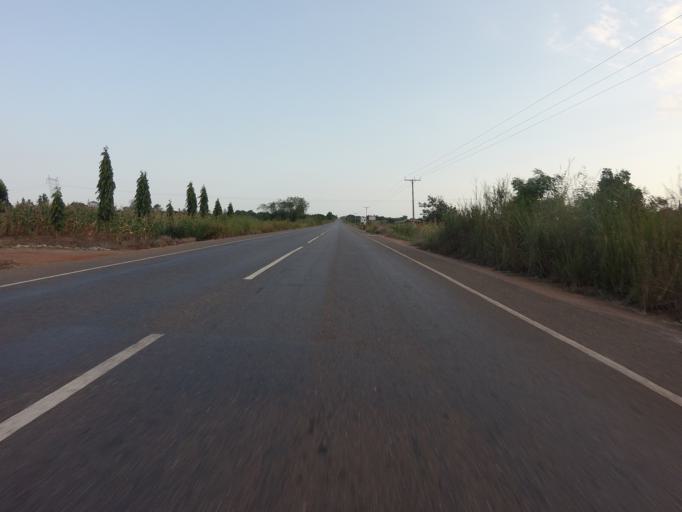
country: GH
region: Volta
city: Anloga
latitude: 6.0713
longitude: 0.6045
